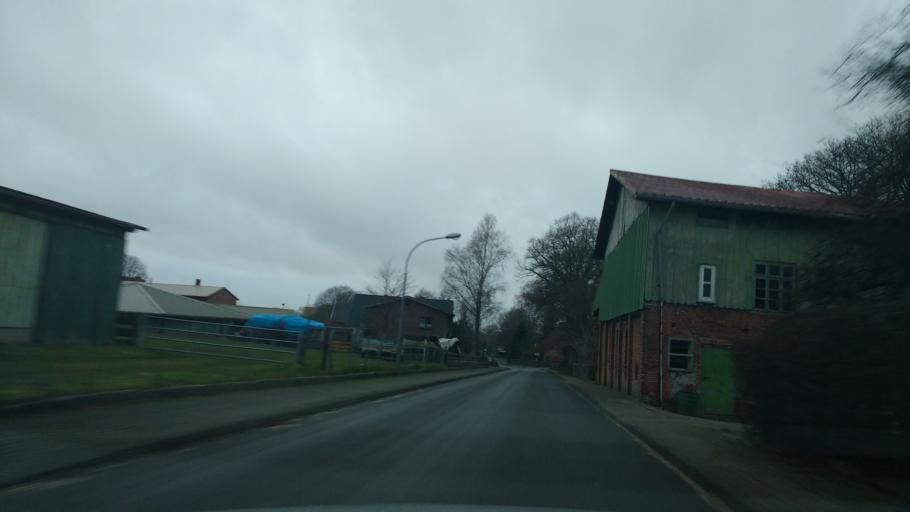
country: DE
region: Schleswig-Holstein
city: Nindorf
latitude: 54.1301
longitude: 9.7025
